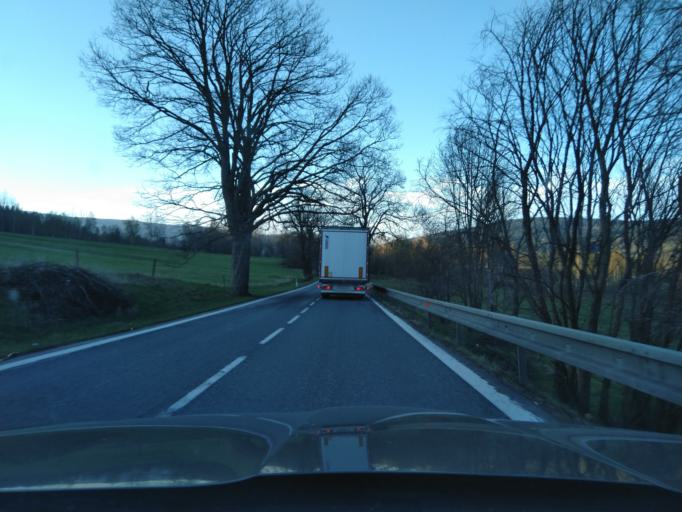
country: CZ
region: Jihocesky
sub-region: Okres Prachatice
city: Vimperk
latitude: 49.0334
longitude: 13.7623
